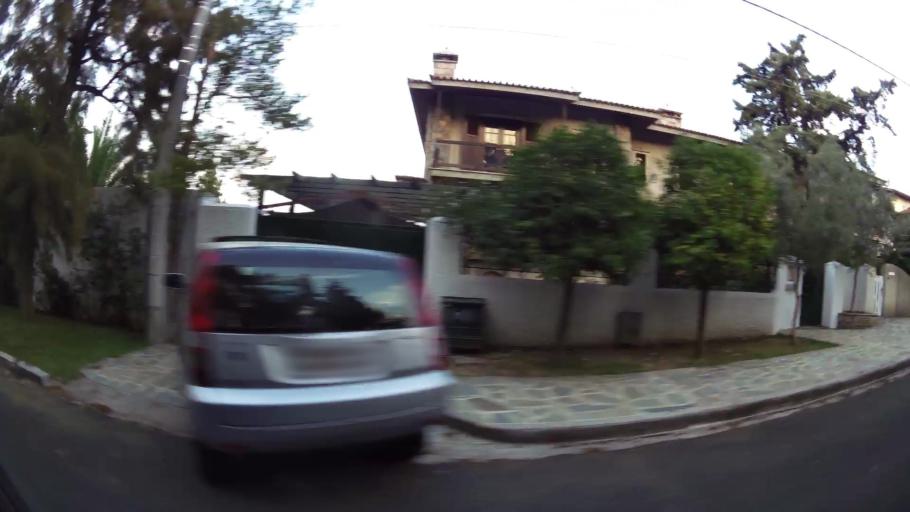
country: GR
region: Attica
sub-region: Nomarchia Athinas
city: Psychiko
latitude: 38.0216
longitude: 23.7690
